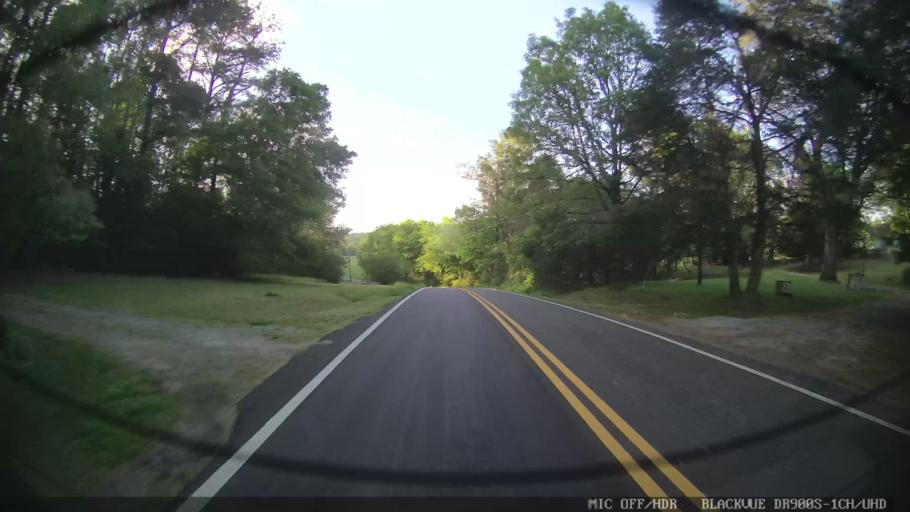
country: US
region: Georgia
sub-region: Bartow County
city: Cartersville
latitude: 34.1326
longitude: -84.8072
